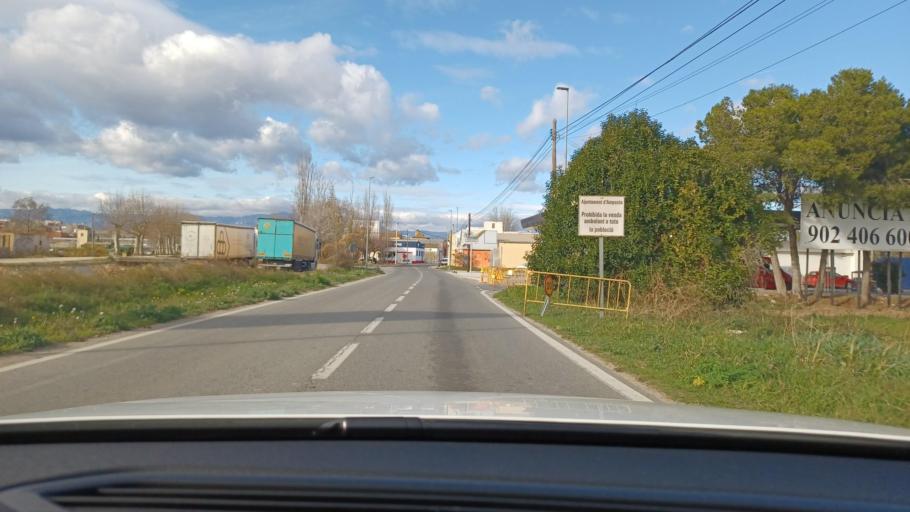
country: ES
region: Catalonia
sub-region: Provincia de Tarragona
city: Amposta
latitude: 40.7087
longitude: 0.5886
